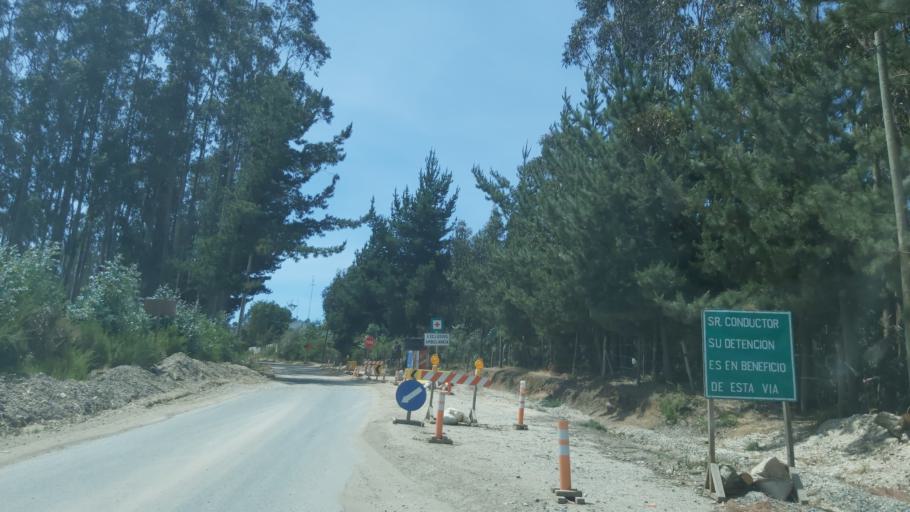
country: CL
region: Maule
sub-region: Provincia de Talca
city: Constitucion
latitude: -35.4393
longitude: -72.4555
